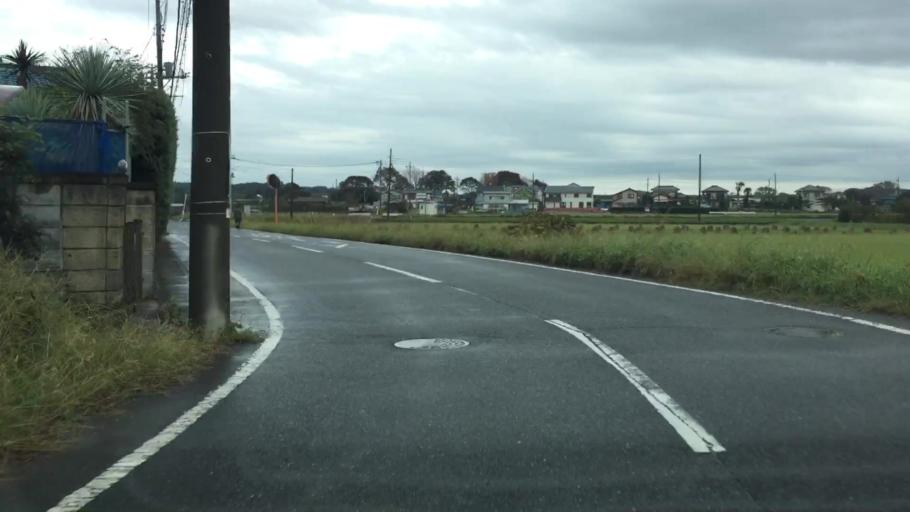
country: JP
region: Ibaraki
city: Toride
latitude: 35.8658
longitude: 140.1166
